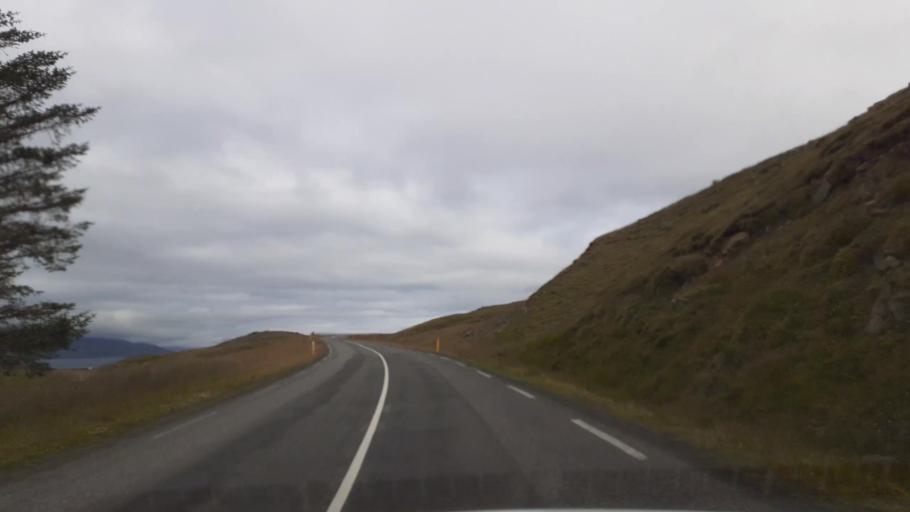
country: IS
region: Northeast
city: Akureyri
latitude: 65.8224
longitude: -18.0511
